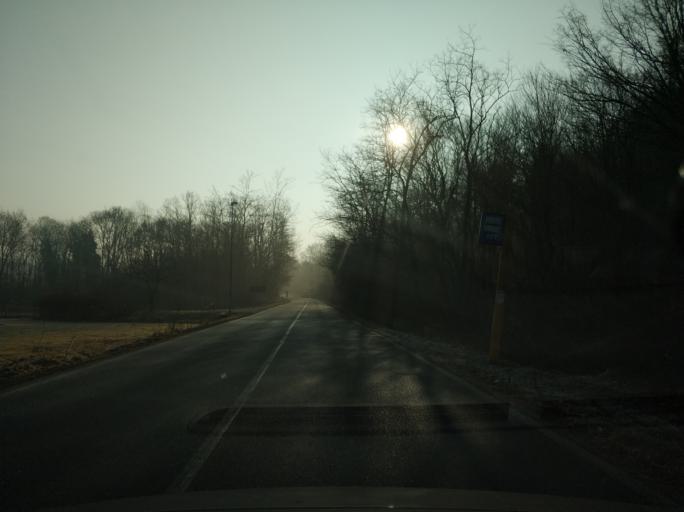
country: IT
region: Piedmont
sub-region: Provincia di Torino
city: Rivarossa
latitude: 45.2564
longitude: 7.7051
